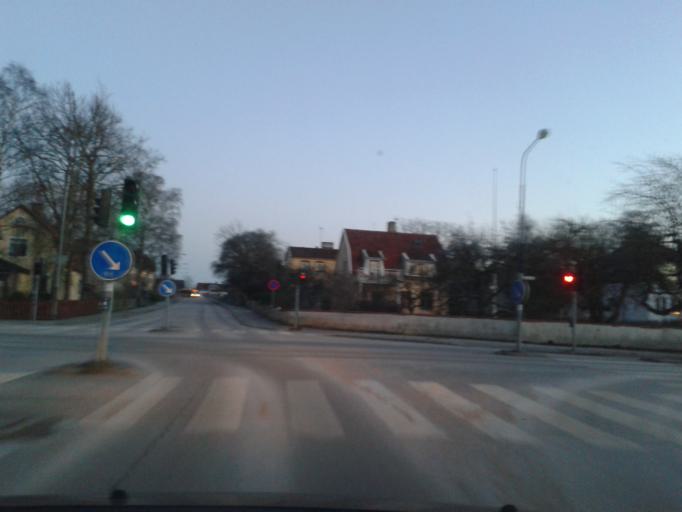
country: SE
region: Gotland
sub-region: Gotland
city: Visby
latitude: 57.6267
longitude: 18.2823
